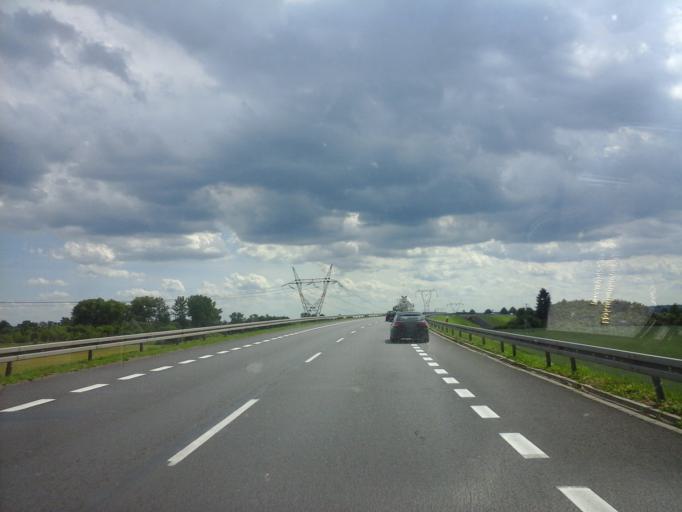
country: PL
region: West Pomeranian Voivodeship
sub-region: Powiat bialogardzki
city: Karlino
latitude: 54.0367
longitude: 15.8971
